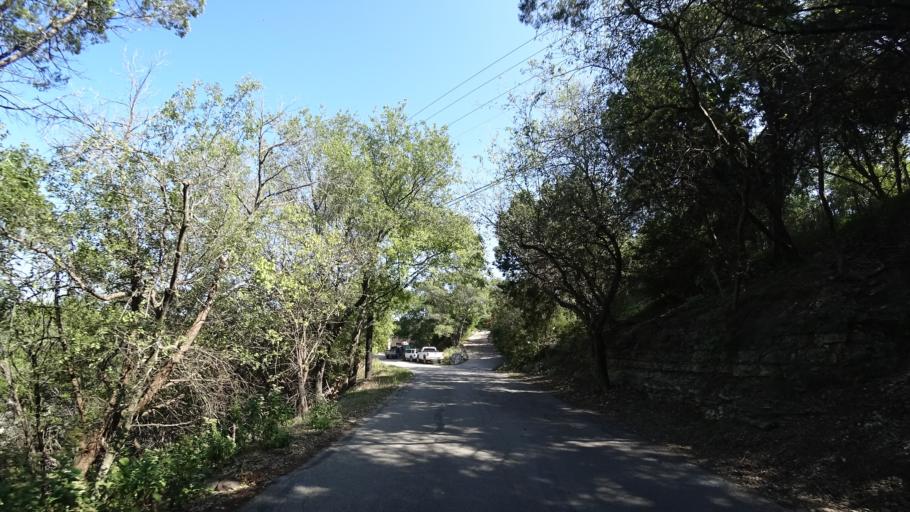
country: US
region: Texas
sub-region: Travis County
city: West Lake Hills
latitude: 30.3044
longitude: -97.8054
